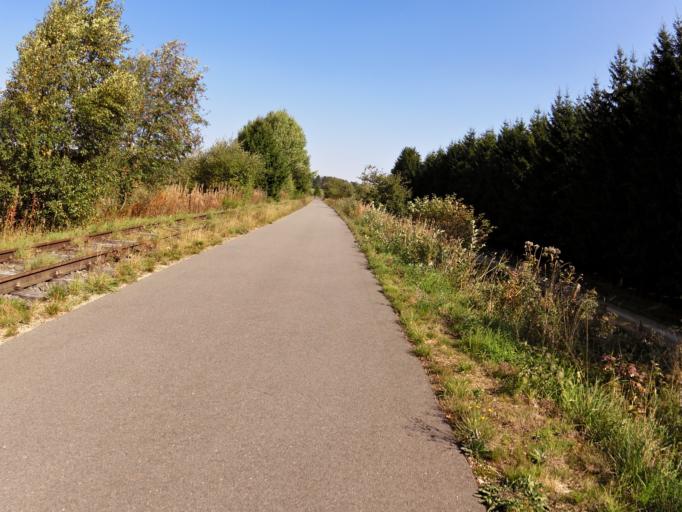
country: BE
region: Wallonia
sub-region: Province de Liege
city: Butgenbach
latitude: 50.4830
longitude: 6.1571
